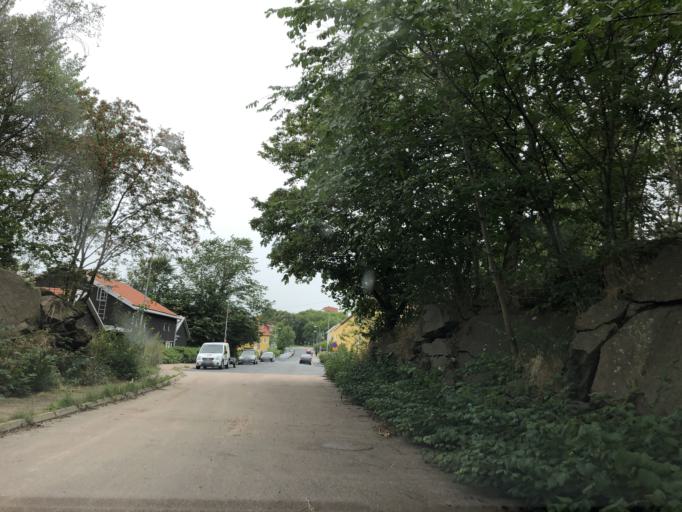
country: SE
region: Vaestra Goetaland
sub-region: Goteborg
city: Majorna
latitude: 57.7122
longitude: 11.9207
